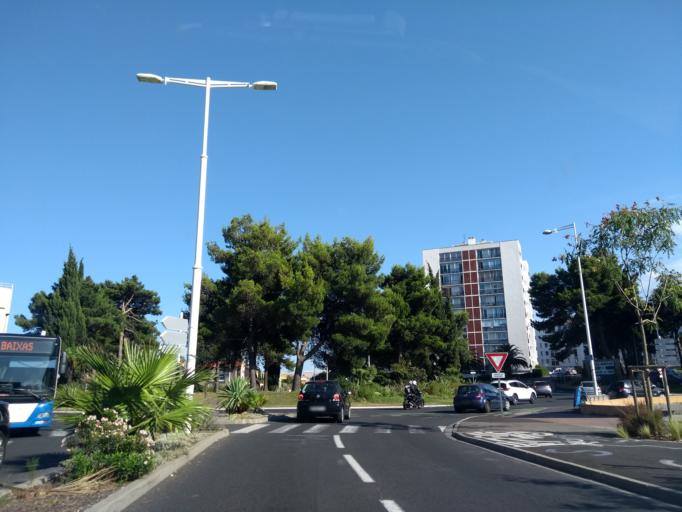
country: FR
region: Languedoc-Roussillon
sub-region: Departement des Pyrenees-Orientales
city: Perpignan
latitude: 42.6868
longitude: 2.9065
